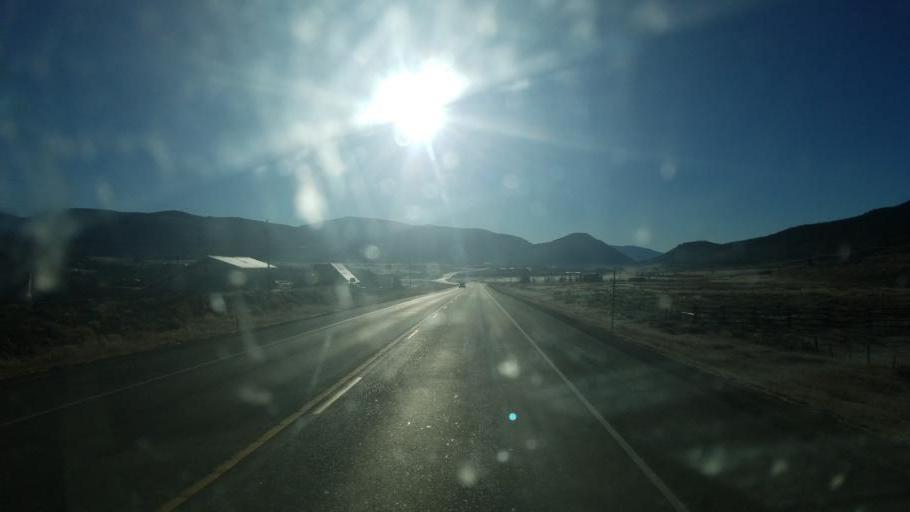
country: US
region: Colorado
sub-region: Gunnison County
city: Crested Butte
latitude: 38.8588
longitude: -106.9679
